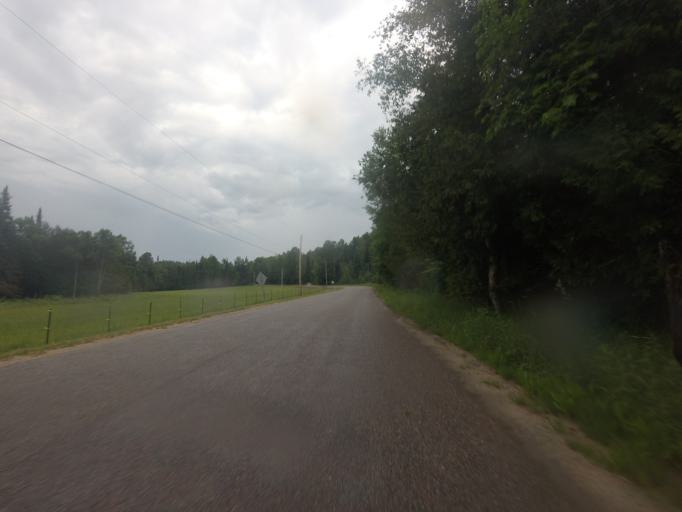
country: CA
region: Quebec
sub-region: Outaouais
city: Maniwaki
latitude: 46.4422
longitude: -75.9367
